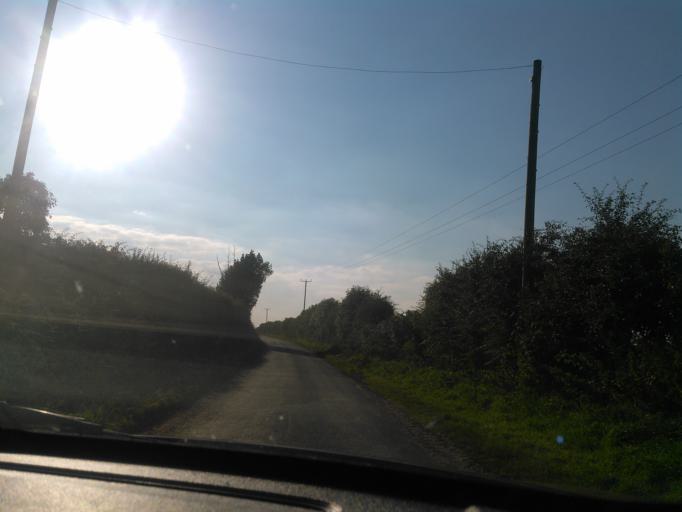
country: GB
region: England
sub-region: Shropshire
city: Stoke upon Tern
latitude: 52.8175
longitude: -2.5907
